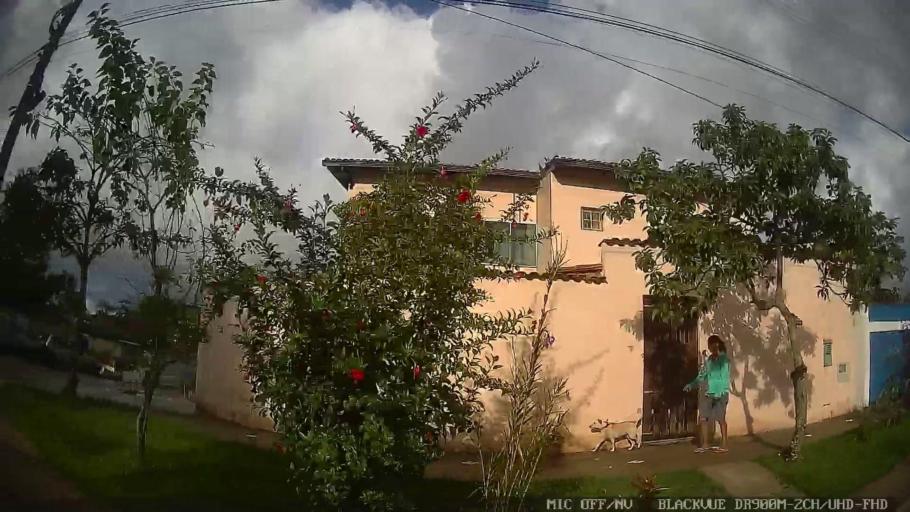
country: BR
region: Sao Paulo
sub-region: Itanhaem
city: Itanhaem
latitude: -24.1999
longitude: -46.8701
